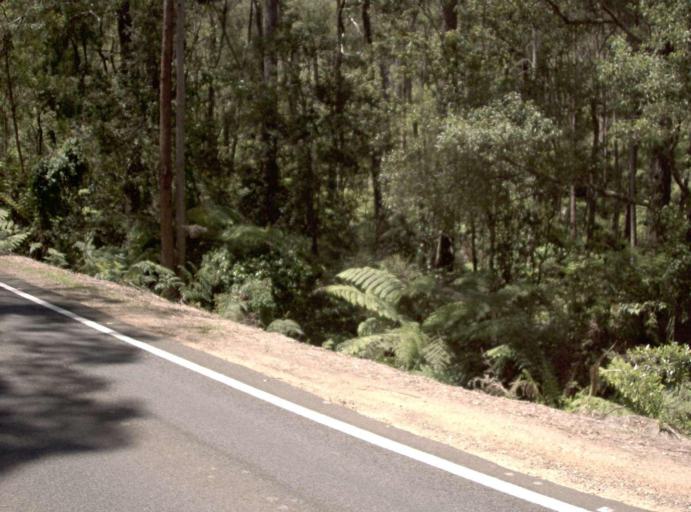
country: AU
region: New South Wales
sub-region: Bombala
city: Bombala
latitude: -37.5898
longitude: 148.9186
